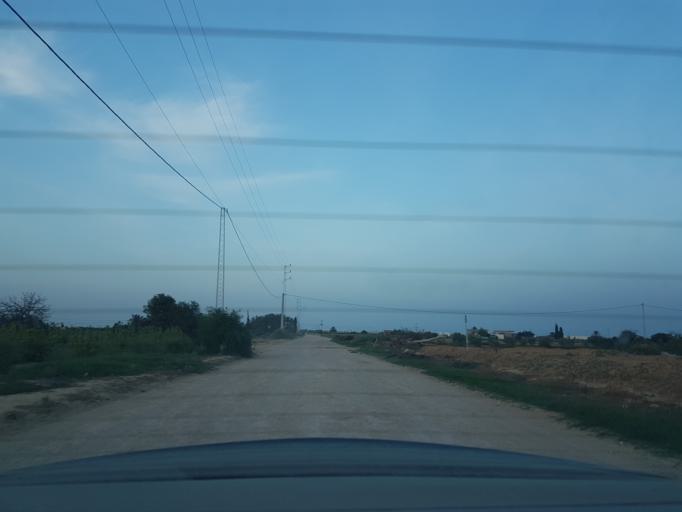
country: TN
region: Safaqis
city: Sfax
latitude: 34.7049
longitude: 10.6830
